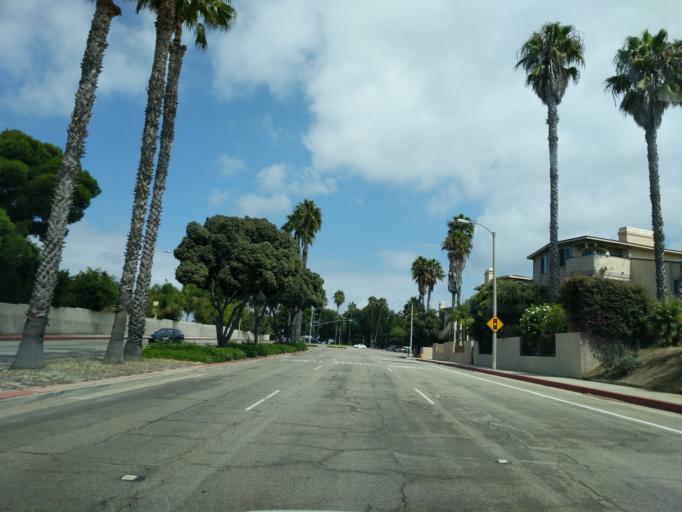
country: US
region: California
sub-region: Orange County
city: Seal Beach
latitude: 33.7134
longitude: -118.0502
